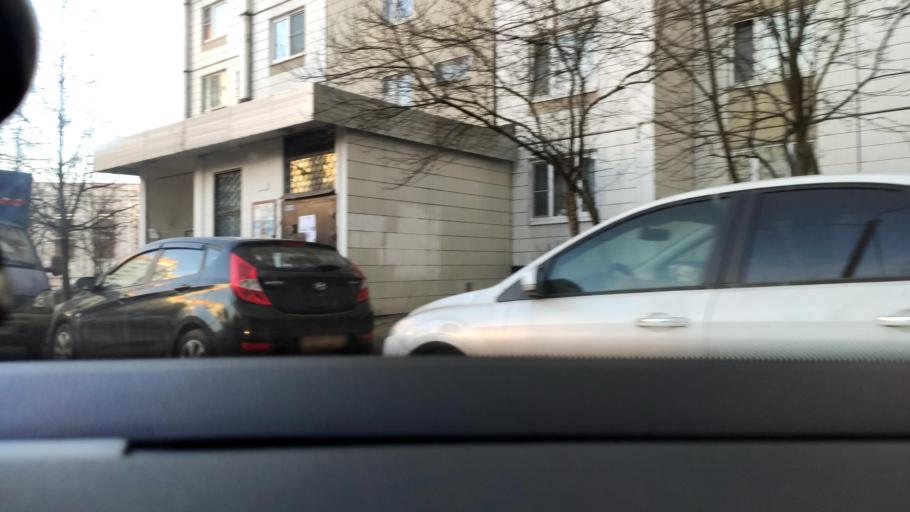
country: RU
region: Moscow
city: Strogino
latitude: 55.8416
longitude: 37.3867
